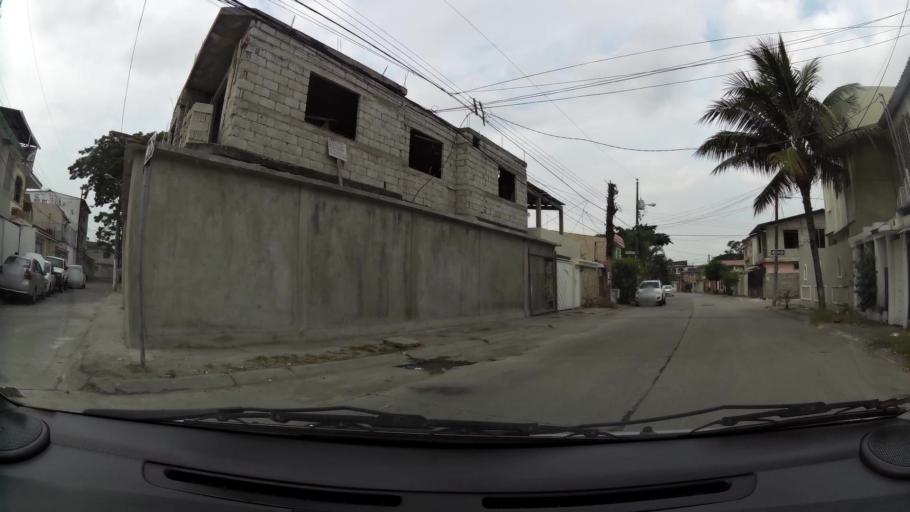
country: EC
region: Guayas
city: Eloy Alfaro
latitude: -2.1150
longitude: -79.8949
